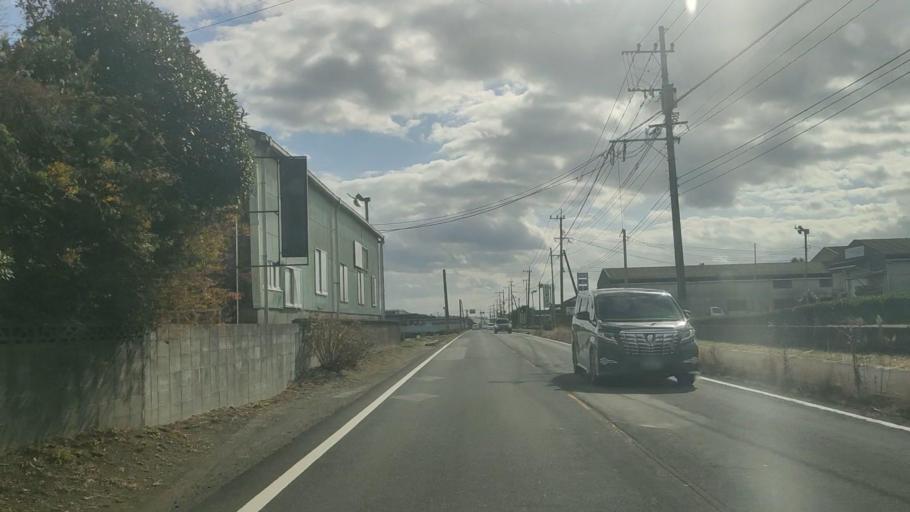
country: JP
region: Kagoshima
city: Kajiki
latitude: 31.8106
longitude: 130.7088
